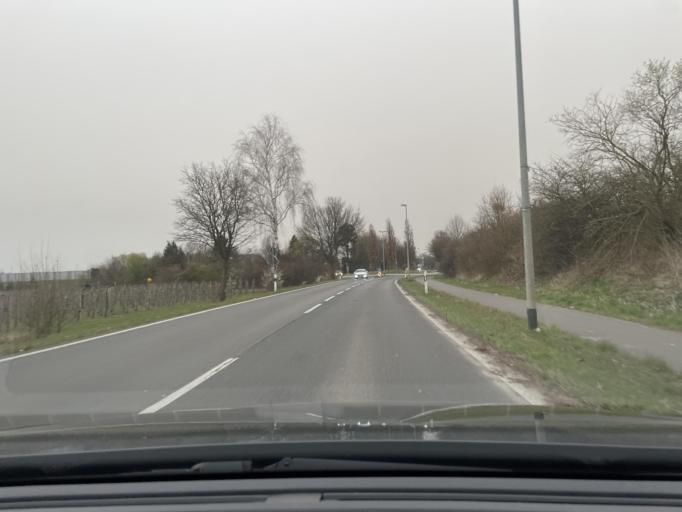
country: DE
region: North Rhine-Westphalia
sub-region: Regierungsbezirk Dusseldorf
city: Juchen
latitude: 51.1069
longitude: 6.4491
